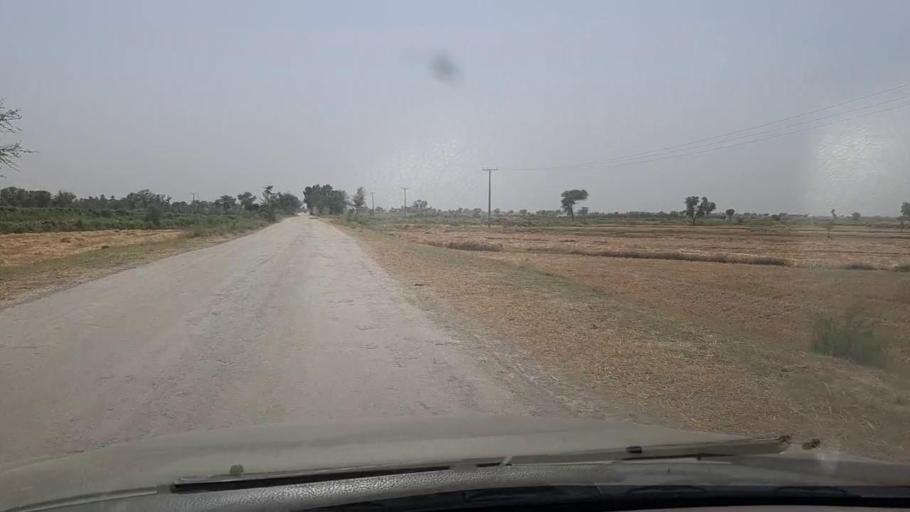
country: PK
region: Sindh
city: Miro Khan
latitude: 27.7188
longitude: 68.0680
